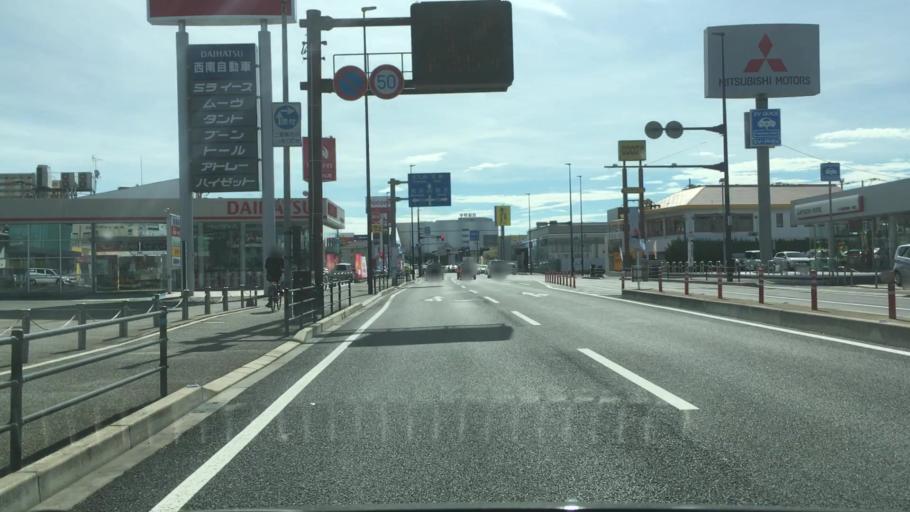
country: JP
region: Fukuoka
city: Fukuoka-shi
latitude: 33.5682
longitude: 130.3214
